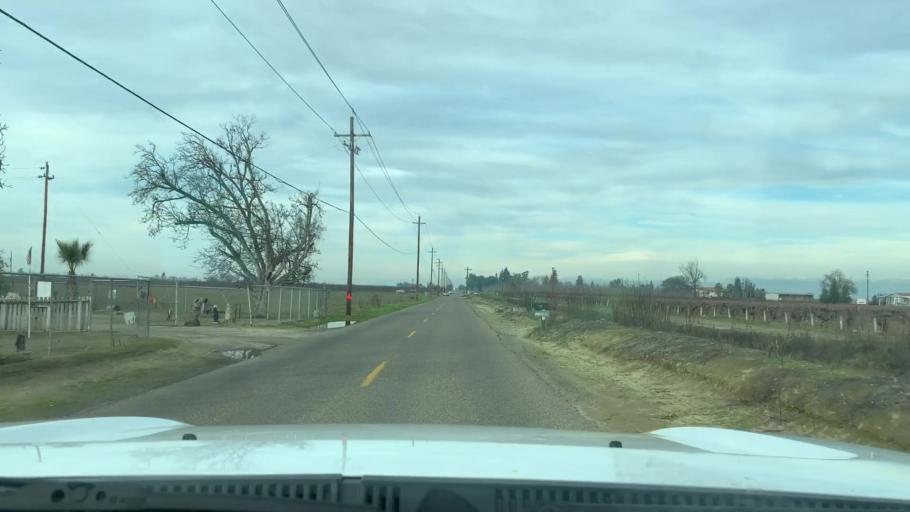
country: US
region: California
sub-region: Fresno County
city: Selma
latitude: 36.5722
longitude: -119.5750
